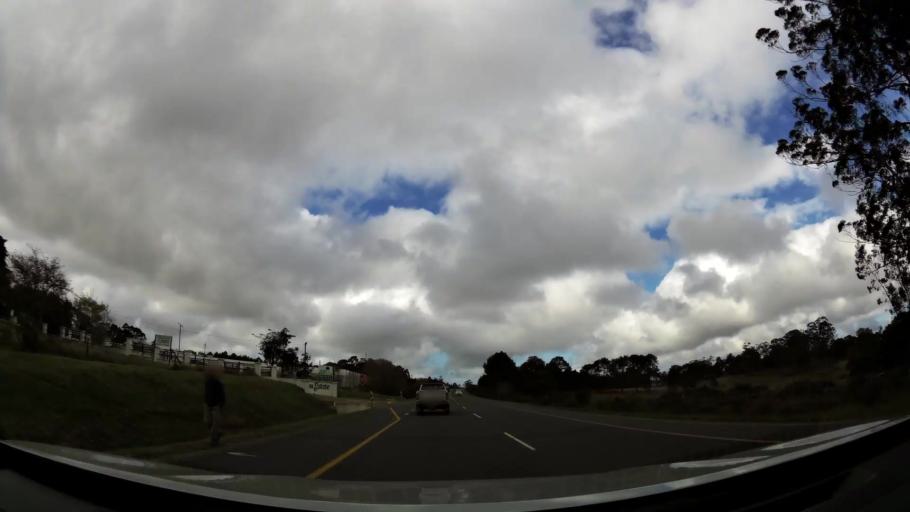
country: ZA
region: Western Cape
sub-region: Eden District Municipality
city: Plettenberg Bay
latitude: -34.0381
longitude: 23.2375
